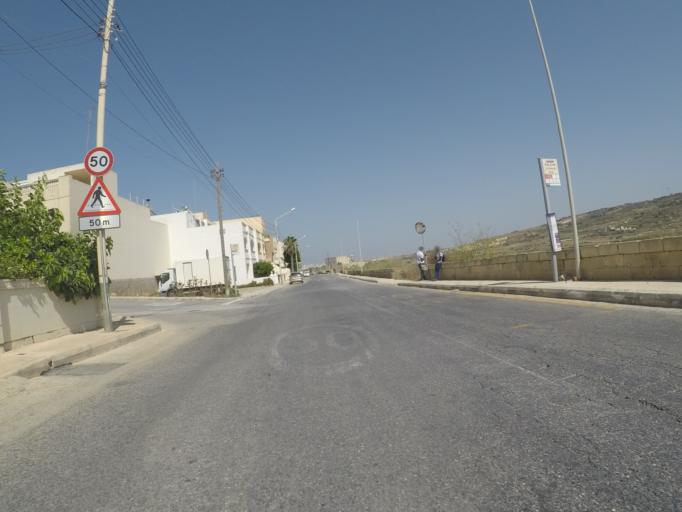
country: MT
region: L-Imgarr
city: Imgarr
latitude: 35.9187
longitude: 14.3761
